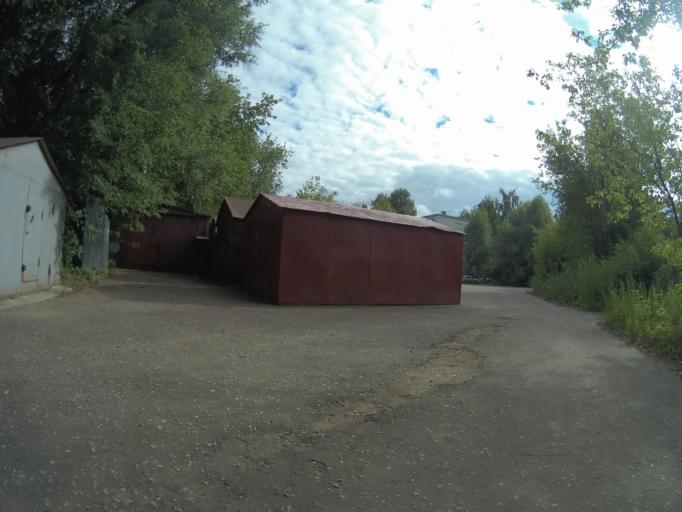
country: RU
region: Vladimir
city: Kommunar
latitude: 56.1485
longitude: 40.4363
